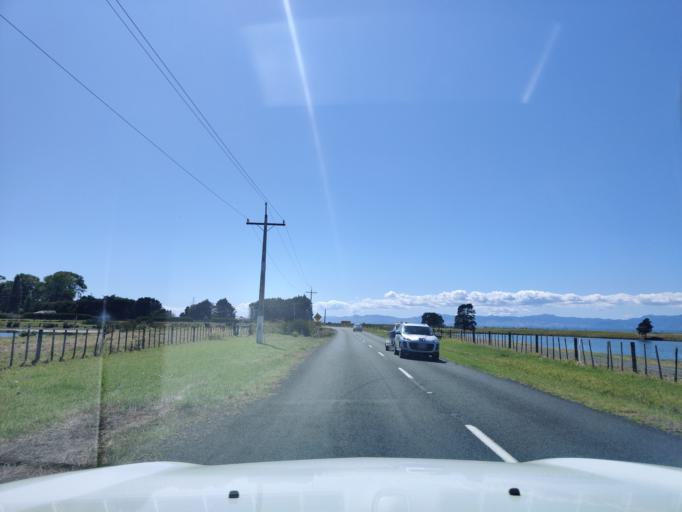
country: NZ
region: Waikato
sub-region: Thames-Coromandel District
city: Thames
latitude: -37.0564
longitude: 175.3009
